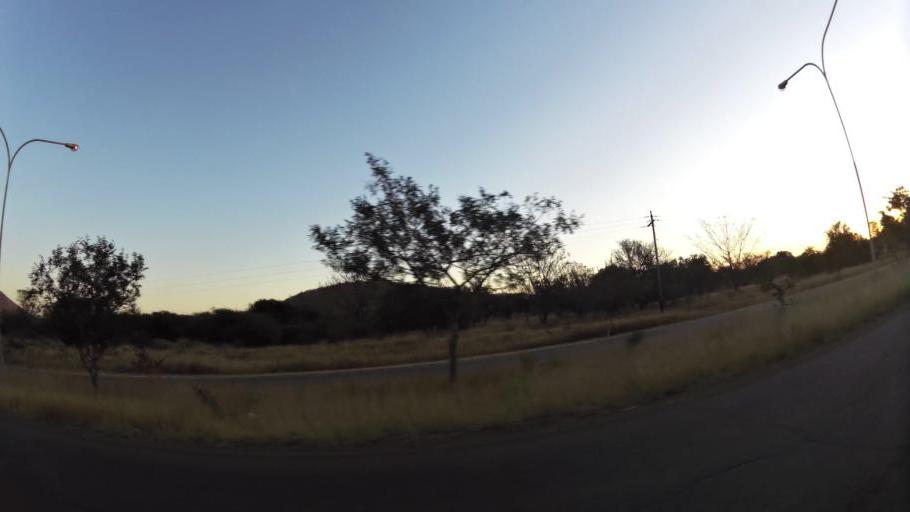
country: ZA
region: North-West
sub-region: Bojanala Platinum District Municipality
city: Rustenburg
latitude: -25.6230
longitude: 27.1840
